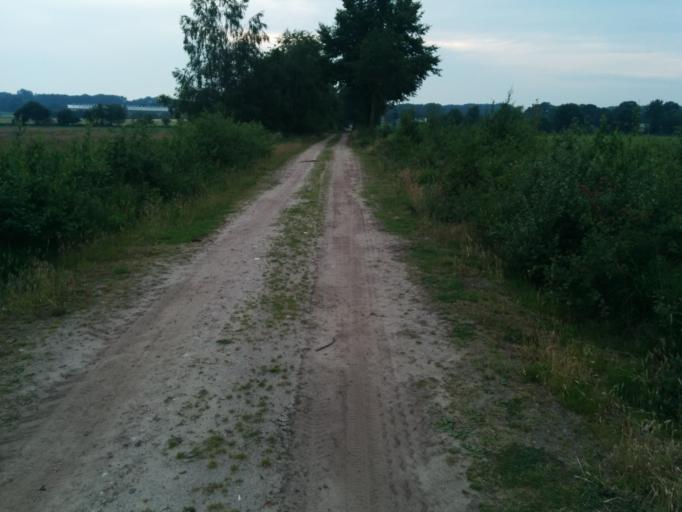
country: DE
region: Lower Saxony
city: Lohne
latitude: 52.6385
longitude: 8.2765
